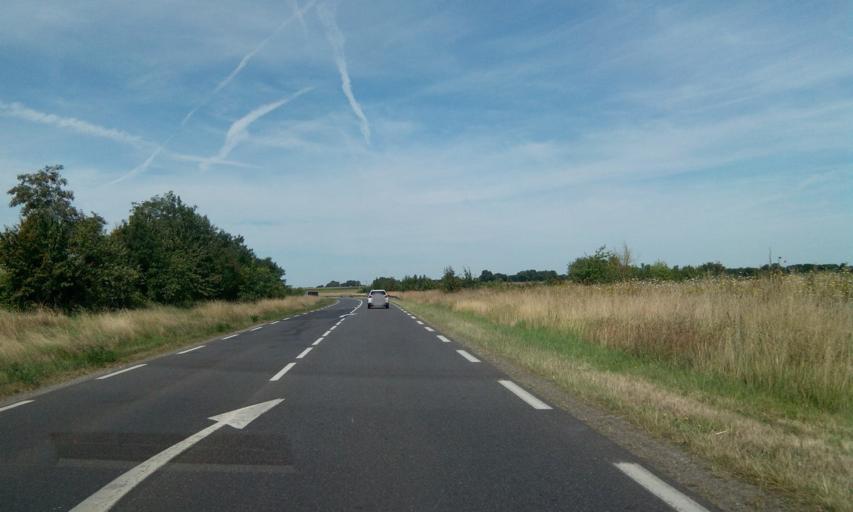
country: FR
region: Poitou-Charentes
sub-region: Departement de la Vienne
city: Charroux
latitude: 46.1520
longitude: 0.4018
